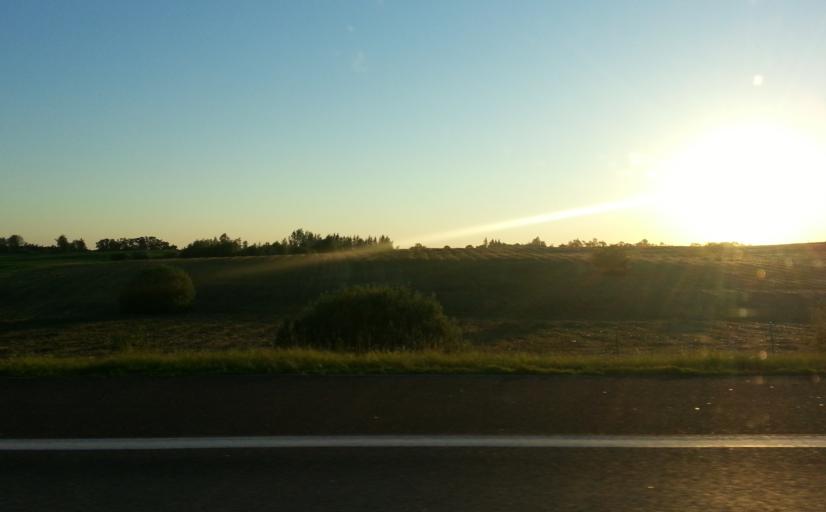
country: LT
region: Vilnius County
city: Ukmerge
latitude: 55.1927
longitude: 24.8125
